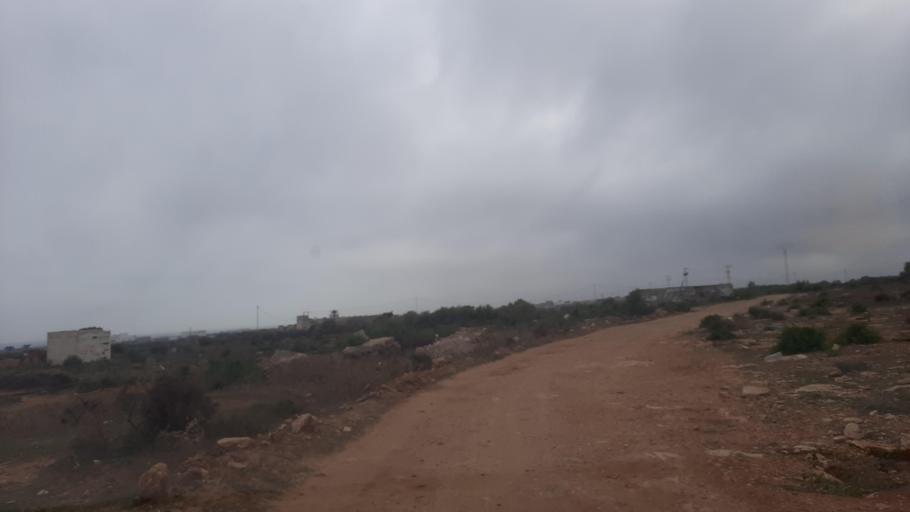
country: TN
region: Nabul
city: Menzel Heurr
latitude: 36.6915
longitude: 10.9348
